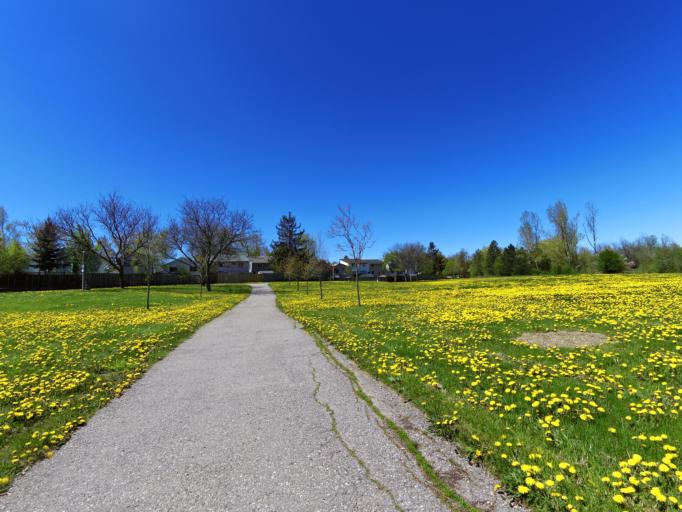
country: CA
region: Ontario
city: Brampton
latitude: 43.7285
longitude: -79.7307
